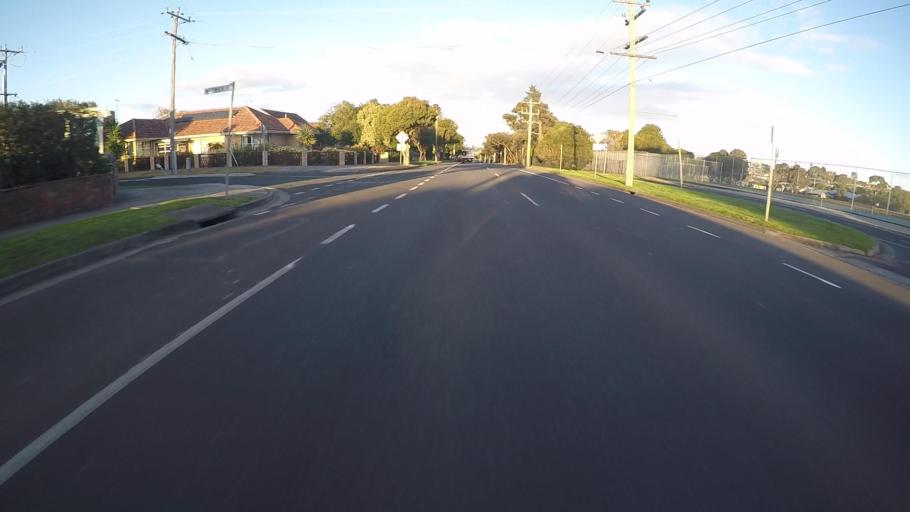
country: AU
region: Victoria
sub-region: Greater Geelong
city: Geelong West
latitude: -38.1442
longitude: 144.3259
